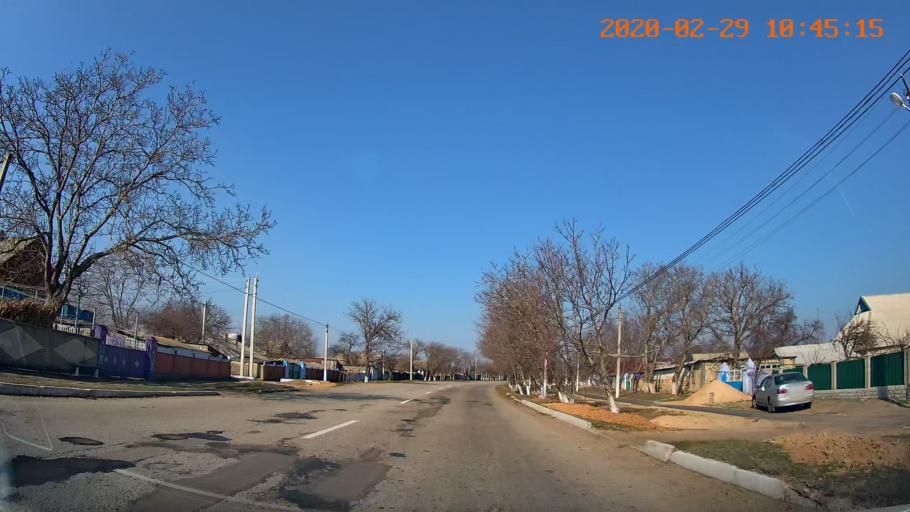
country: MD
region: Telenesti
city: Grigoriopol
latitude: 47.0745
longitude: 29.3851
